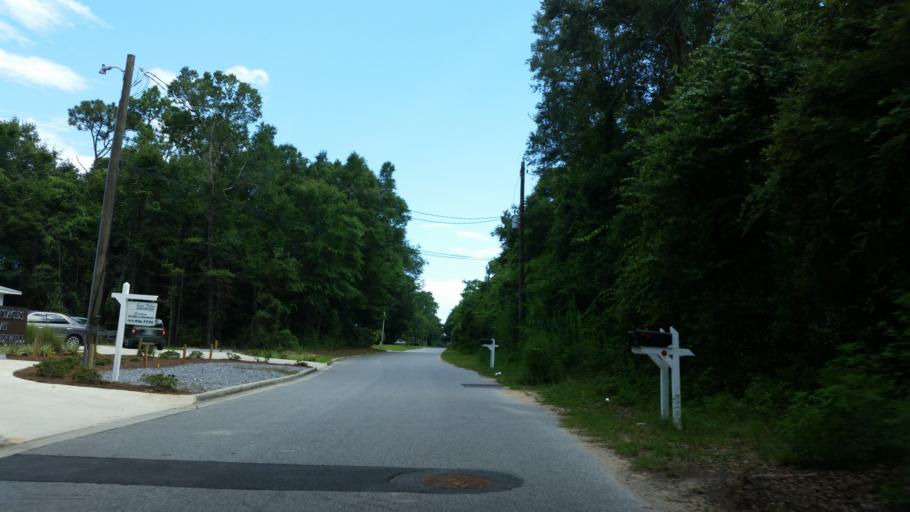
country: US
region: Florida
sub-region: Escambia County
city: Ferry Pass
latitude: 30.5362
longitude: -87.2162
